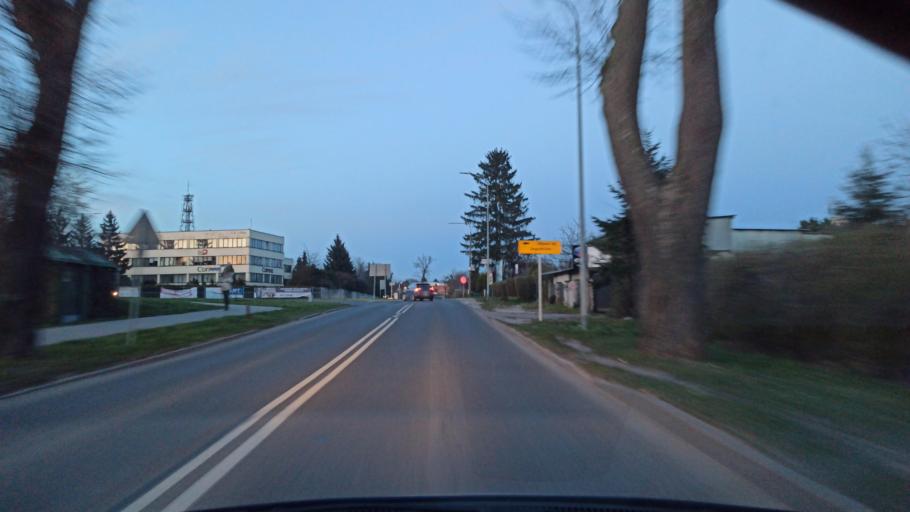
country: PL
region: Warmian-Masurian Voivodeship
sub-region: Powiat elblaski
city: Elblag
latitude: 54.1817
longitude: 19.4326
